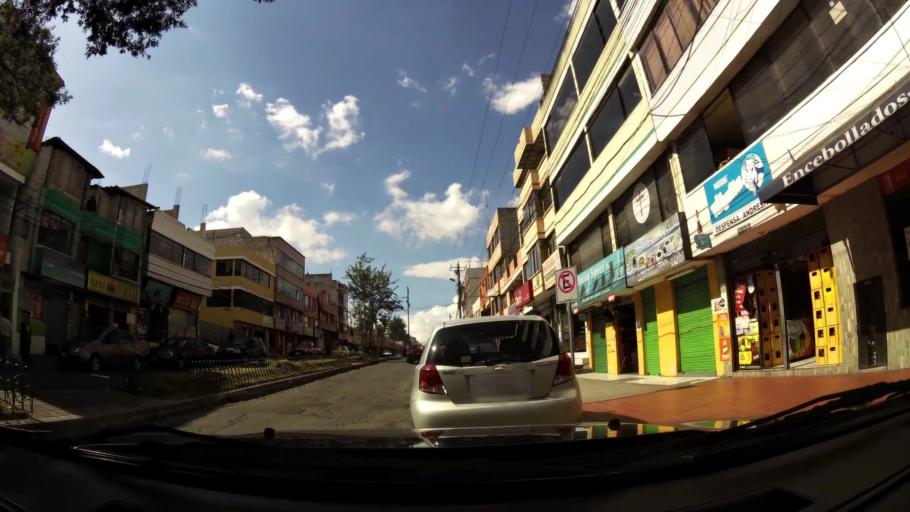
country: EC
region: Pichincha
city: Quito
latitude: -0.1227
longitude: -78.4666
